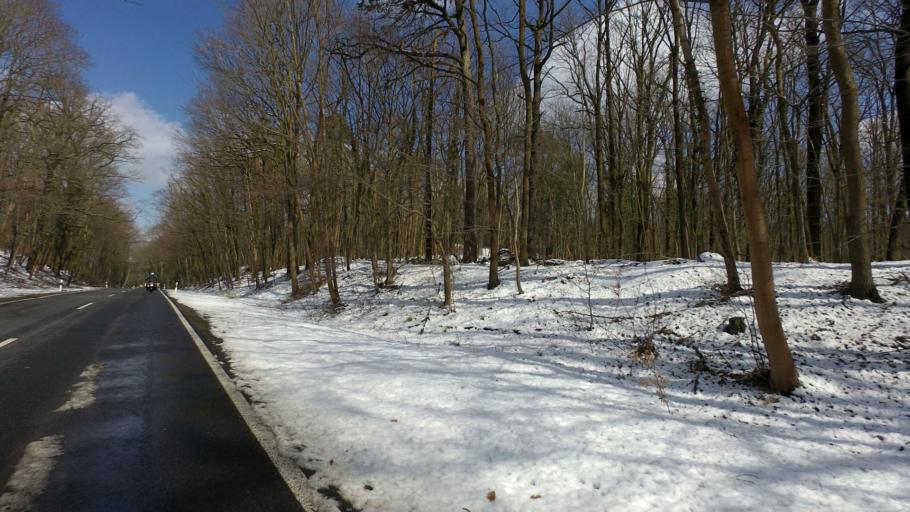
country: DE
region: Brandenburg
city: Eberswalde
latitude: 52.8236
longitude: 13.8314
